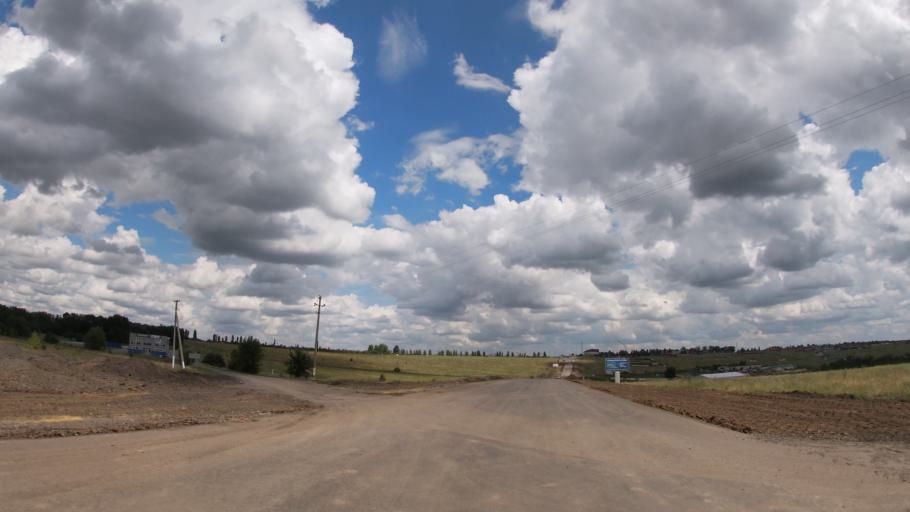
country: RU
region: Belgorod
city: Mayskiy
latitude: 50.5224
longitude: 36.5083
